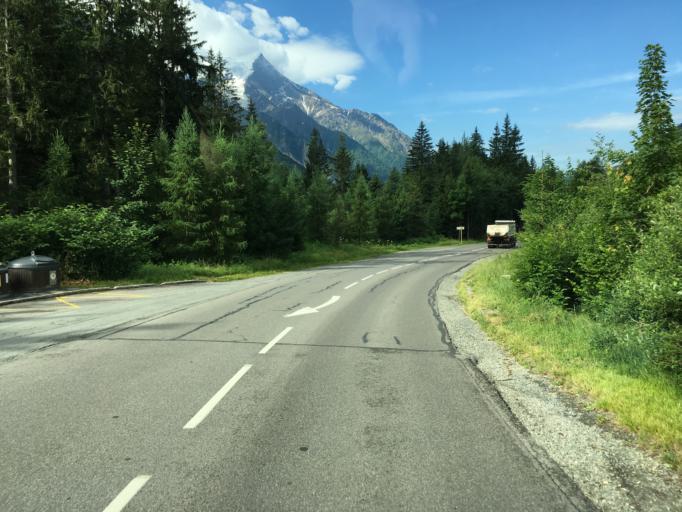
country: FR
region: Rhone-Alpes
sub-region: Departement de la Haute-Savoie
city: Chamonix-Mont-Blanc
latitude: 45.9344
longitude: 6.8889
